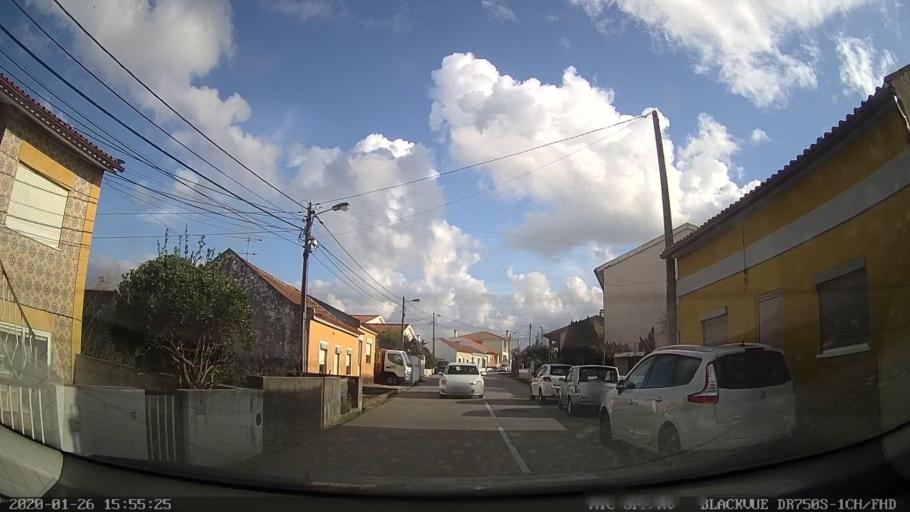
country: PT
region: Aveiro
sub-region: Aveiro
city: Aradas
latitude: 40.6286
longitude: -8.6282
